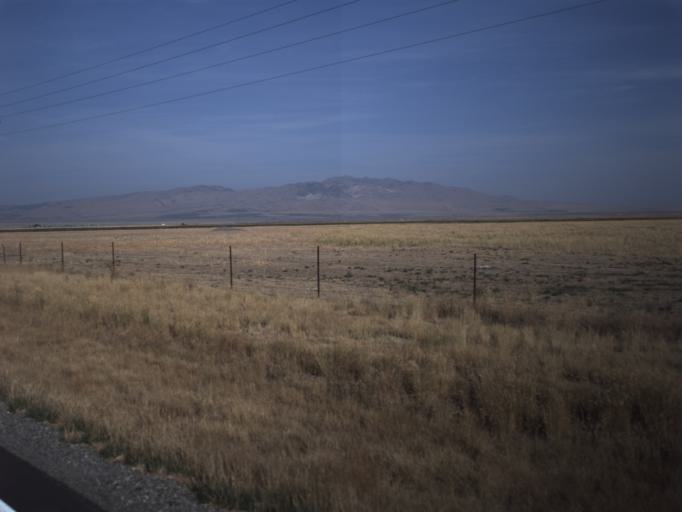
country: US
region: Idaho
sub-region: Oneida County
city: Malad City
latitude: 41.9672
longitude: -112.8494
